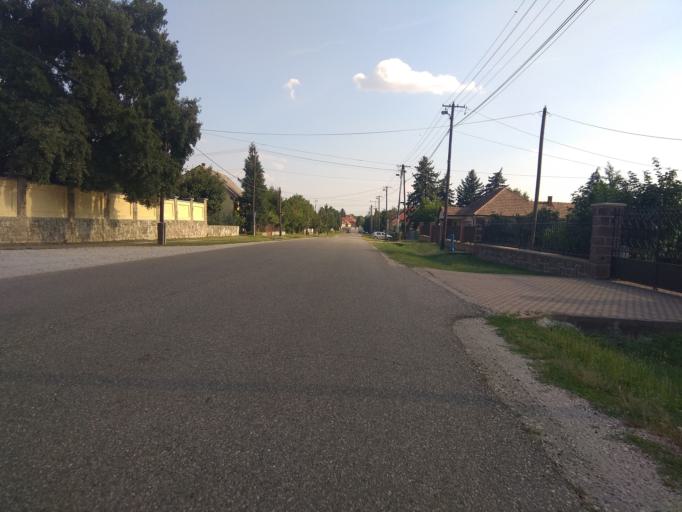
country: HU
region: Borsod-Abauj-Zemplen
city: Mezokeresztes
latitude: 47.8610
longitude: 20.6790
